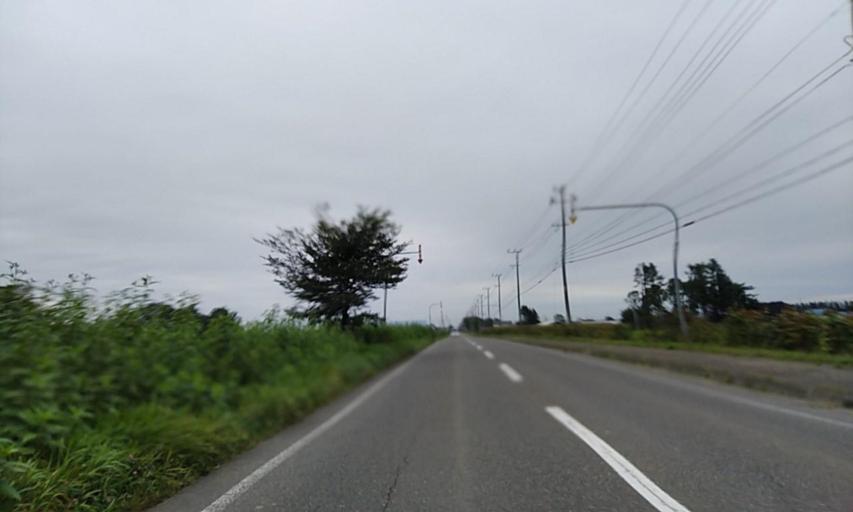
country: JP
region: Hokkaido
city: Obihiro
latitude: 42.6603
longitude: 143.1074
